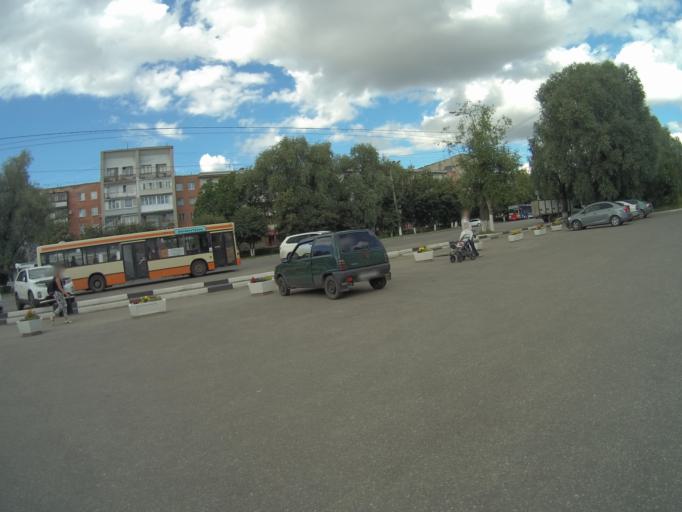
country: RU
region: Vladimir
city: Vladimir
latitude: 56.1196
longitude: 40.3665
